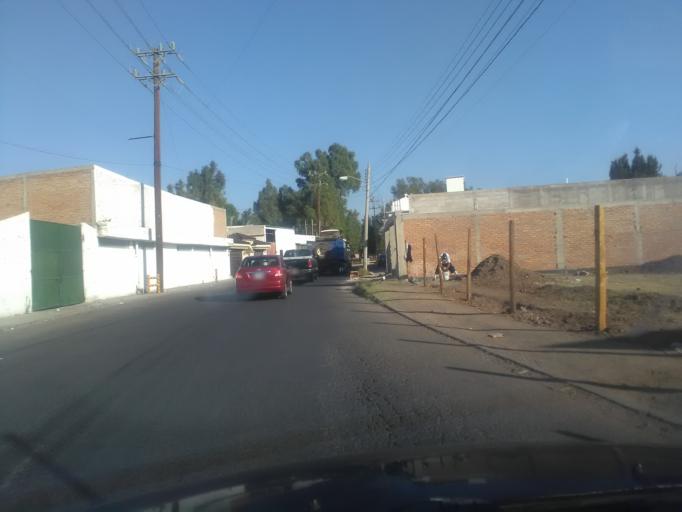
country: MX
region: Durango
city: Victoria de Durango
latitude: 24.0420
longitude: -104.6326
